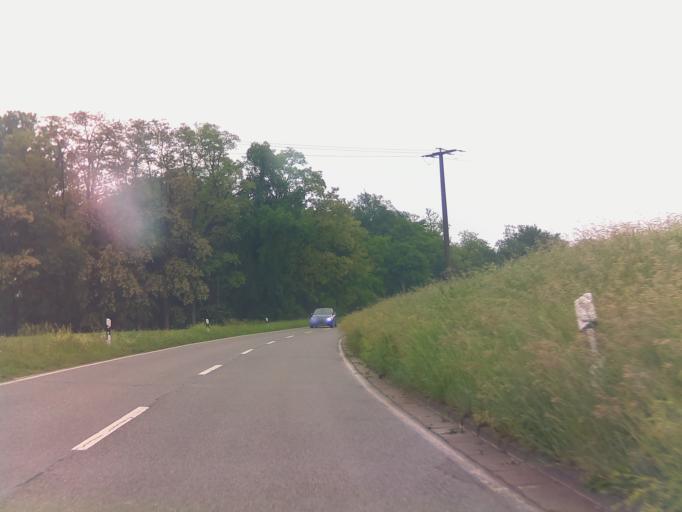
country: DE
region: Rheinland-Pfalz
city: Hordt
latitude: 49.1773
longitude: 8.3165
